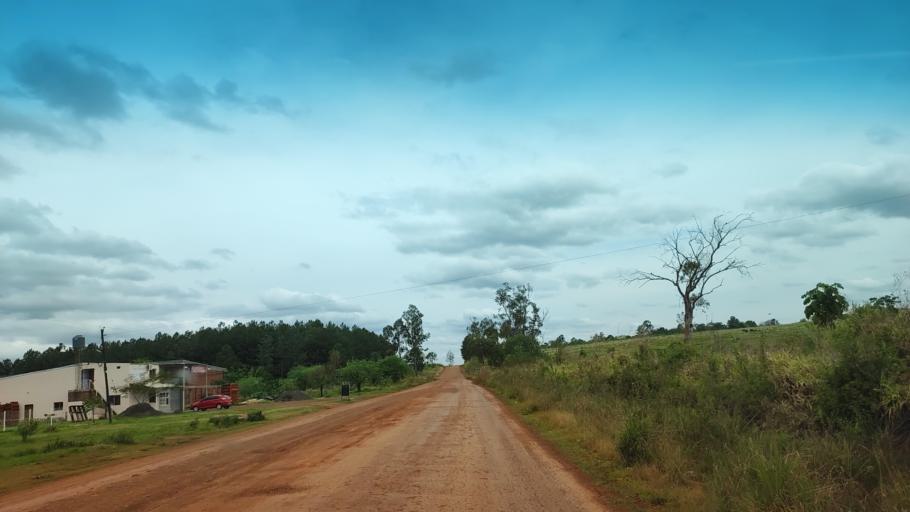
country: AR
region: Misiones
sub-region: Departamento de Capital
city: Posadas
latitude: -27.4796
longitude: -55.9708
